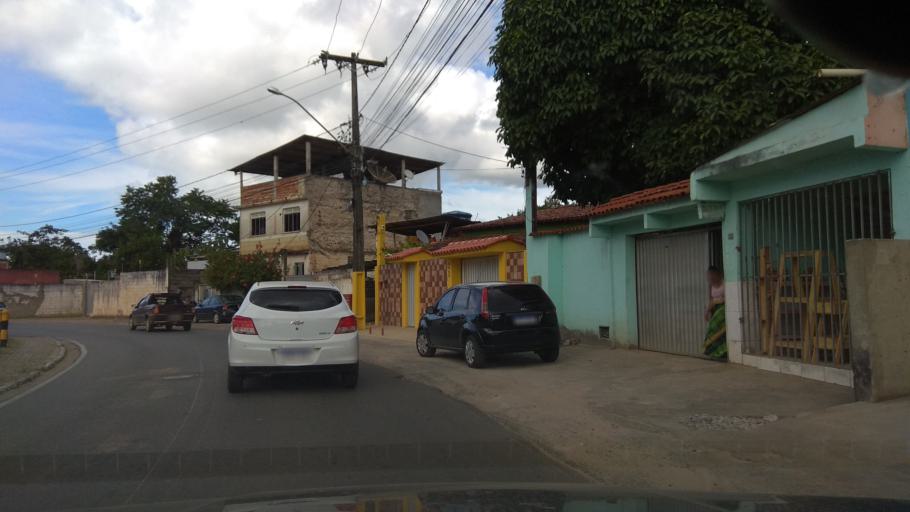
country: BR
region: Bahia
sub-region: Ilheus
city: Ilheus
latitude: -14.7942
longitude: -39.0634
